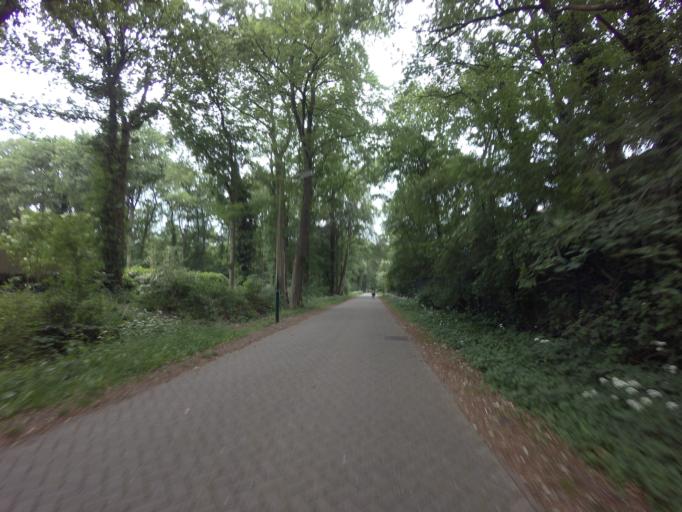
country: NL
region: Utrecht
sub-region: Gemeente De Bilt
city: De Bilt
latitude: 52.1343
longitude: 5.1935
